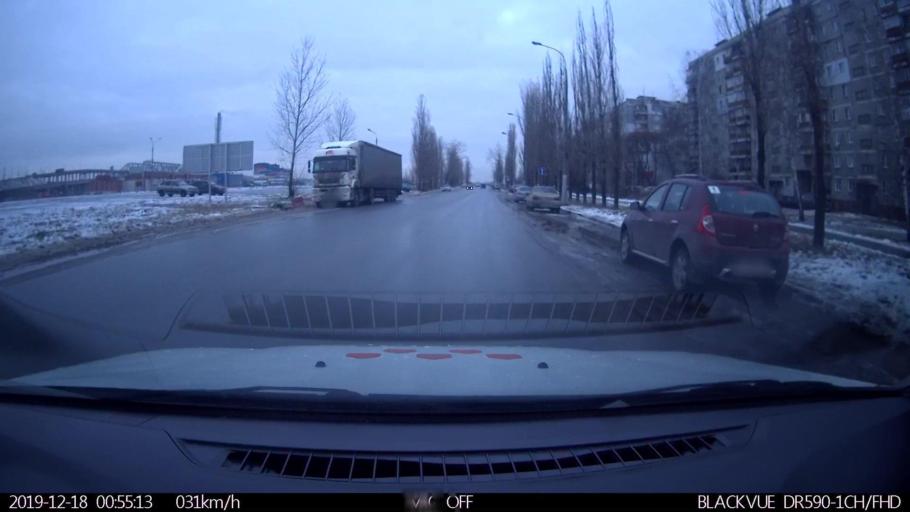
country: RU
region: Nizjnij Novgorod
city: Nizhniy Novgorod
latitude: 56.3463
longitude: 43.9228
